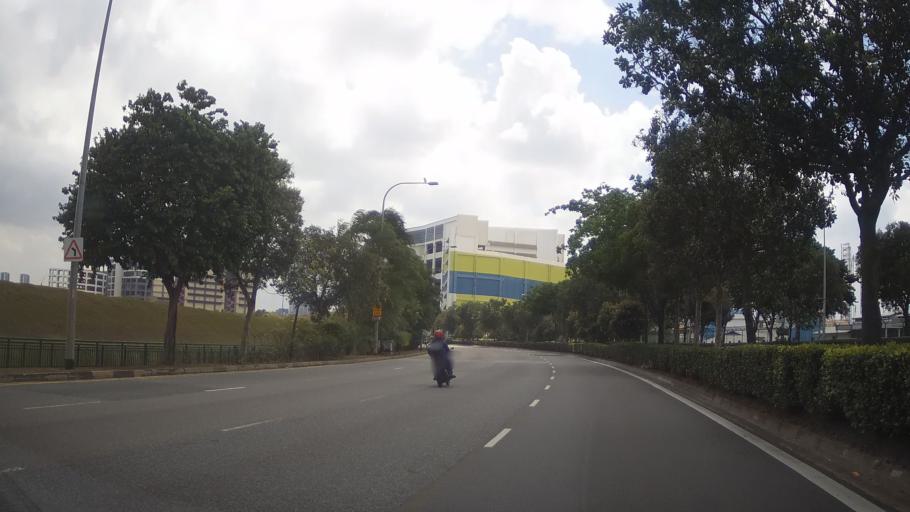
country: SG
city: Singapore
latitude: 1.3040
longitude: 103.7433
